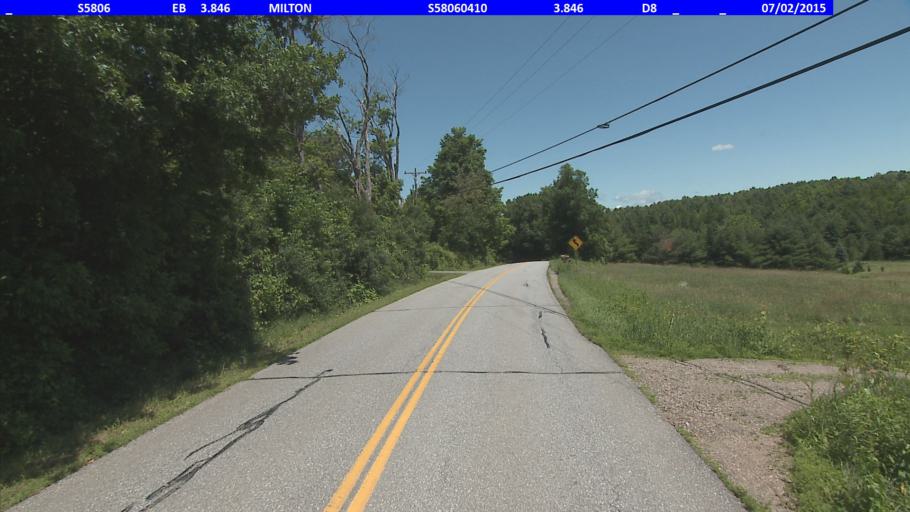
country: US
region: Vermont
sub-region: Chittenden County
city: Milton
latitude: 44.6769
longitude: -73.1749
